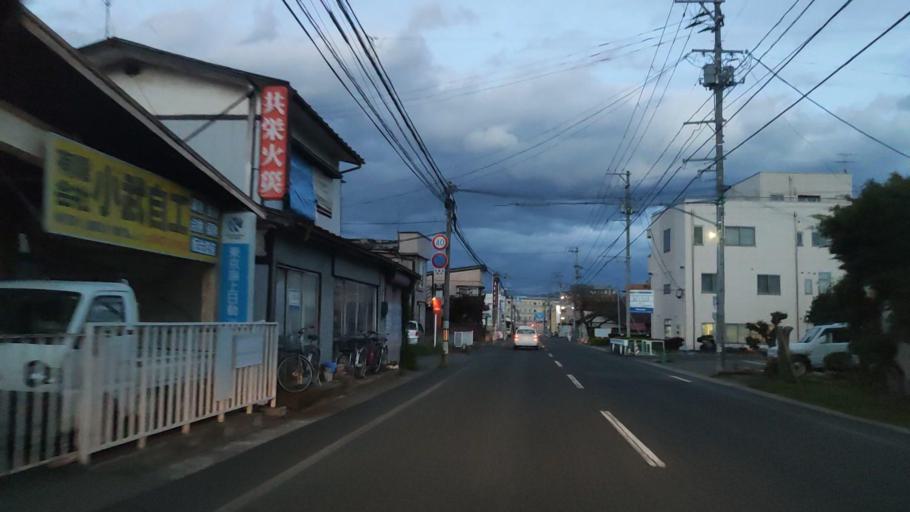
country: JP
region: Iwate
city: Morioka-shi
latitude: 39.7158
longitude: 141.1259
